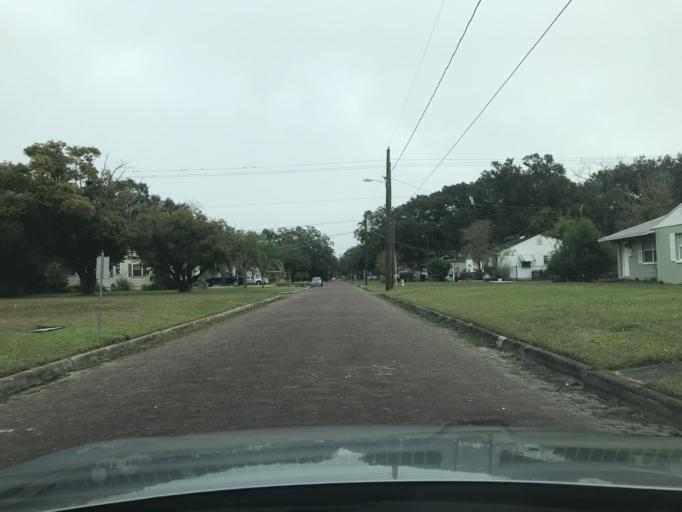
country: US
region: Florida
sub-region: Hillsborough County
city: Tampa
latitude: 27.9798
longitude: -82.4722
